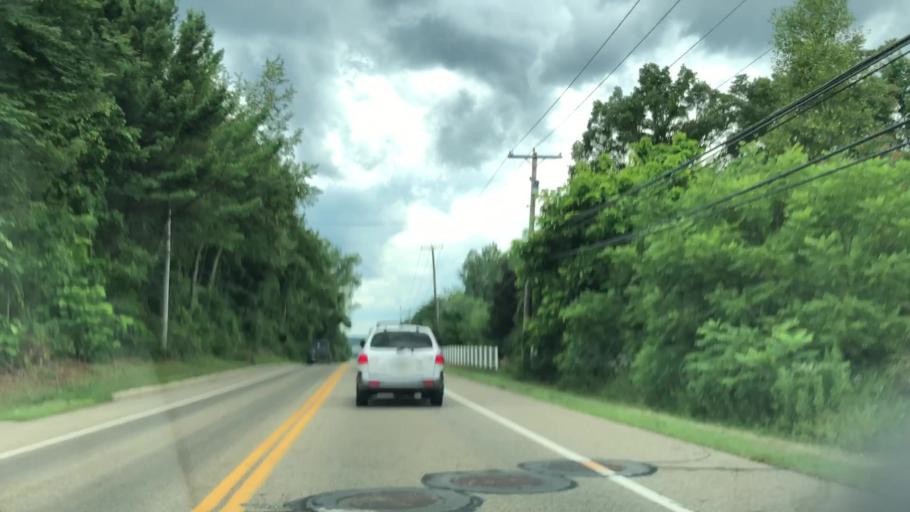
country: US
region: Ohio
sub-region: Summit County
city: Green
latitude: 40.9531
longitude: -81.5036
